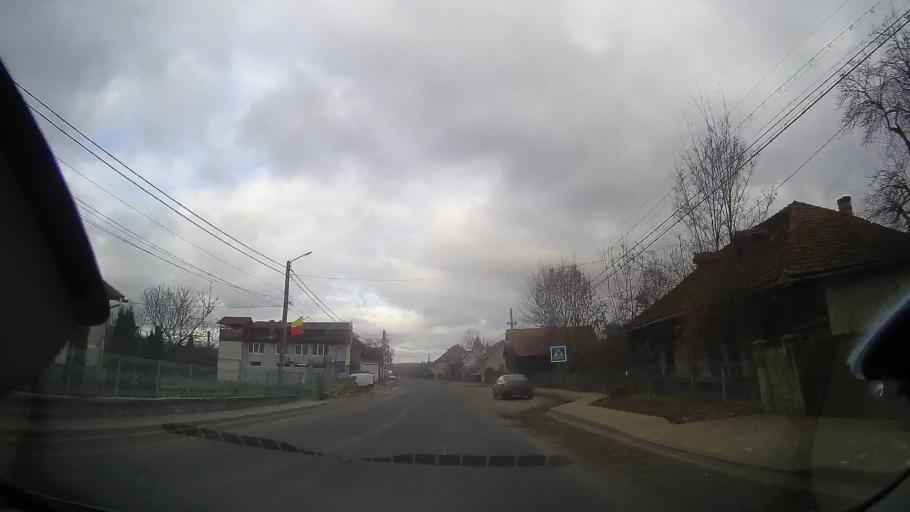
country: RO
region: Cluj
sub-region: Comuna Calatele
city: Calatele
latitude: 46.7647
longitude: 23.0082
